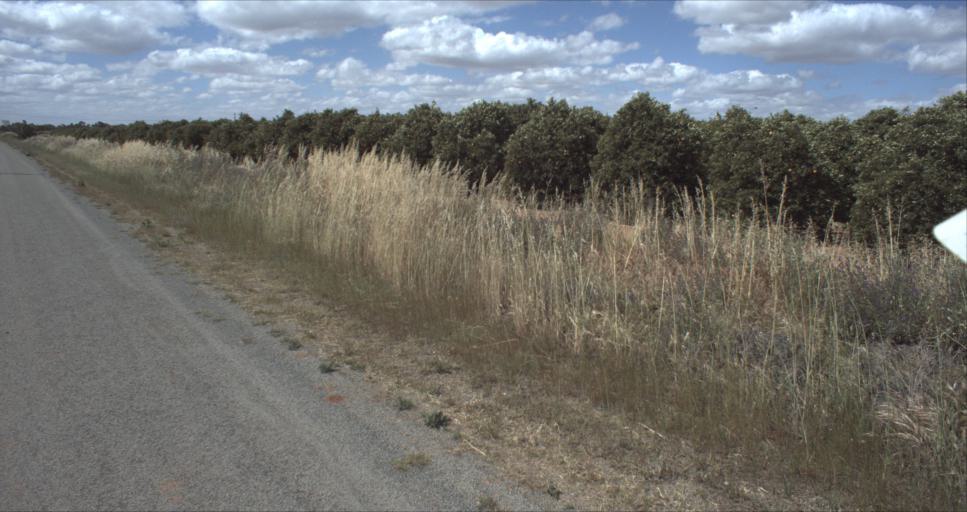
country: AU
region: New South Wales
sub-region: Leeton
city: Leeton
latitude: -34.5823
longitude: 146.3920
